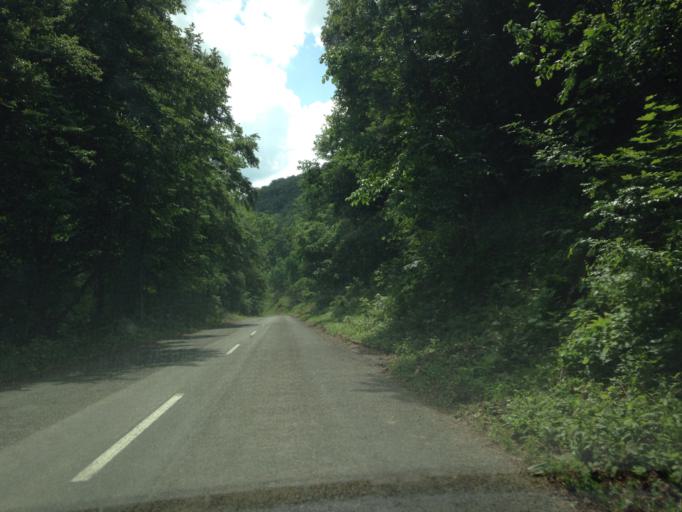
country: HU
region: Pest
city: Visegrad
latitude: 47.7514
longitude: 18.9427
